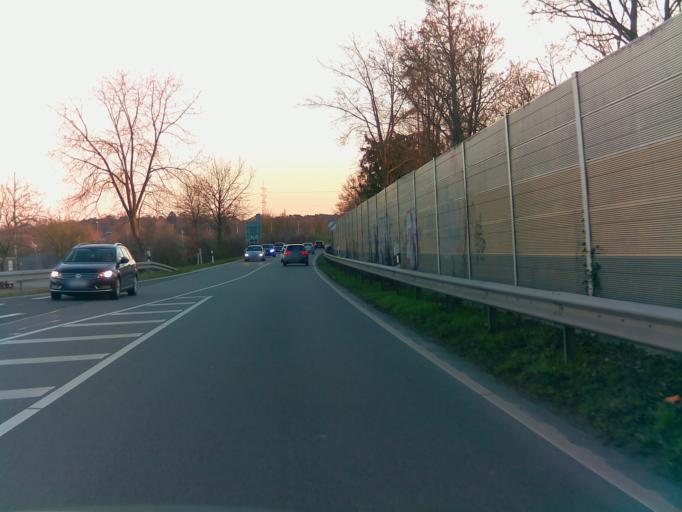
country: DE
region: Baden-Wuerttemberg
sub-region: Karlsruhe Region
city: Sandhausen
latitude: 49.3389
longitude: 8.6658
